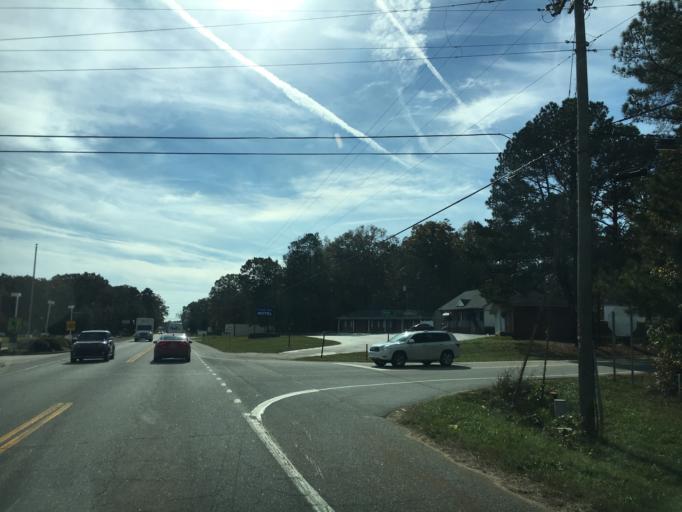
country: US
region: South Carolina
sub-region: Anderson County
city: Anderson
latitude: 34.5217
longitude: -82.5943
